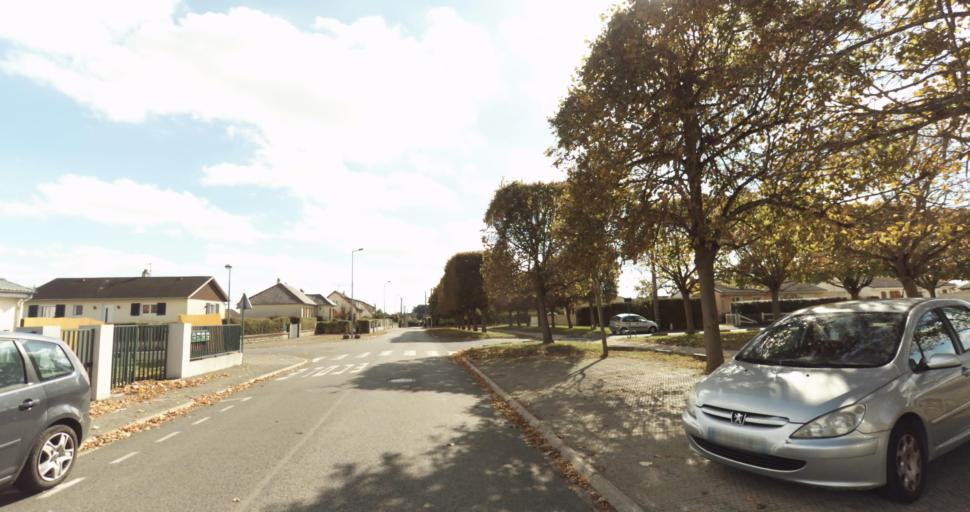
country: FR
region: Centre
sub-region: Departement d'Eure-et-Loir
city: Garnay
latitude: 48.7315
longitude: 1.3342
